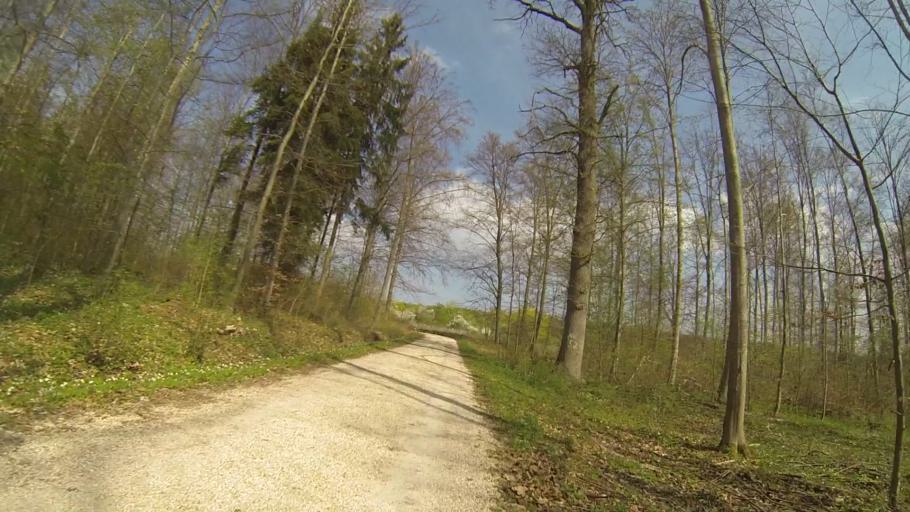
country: DE
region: Baden-Wuerttemberg
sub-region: Regierungsbezirk Stuttgart
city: Heidenheim an der Brenz
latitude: 48.6730
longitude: 10.1869
